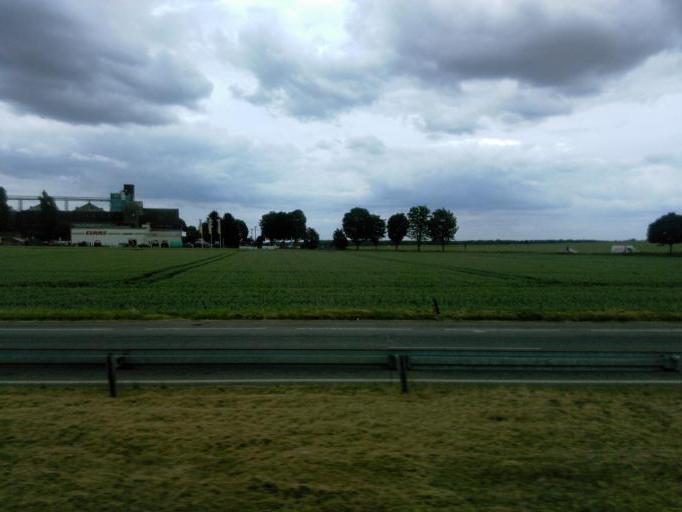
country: FR
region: Ile-de-France
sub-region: Departement du Val-d'Oise
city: Osny
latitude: 49.0910
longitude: 2.0569
